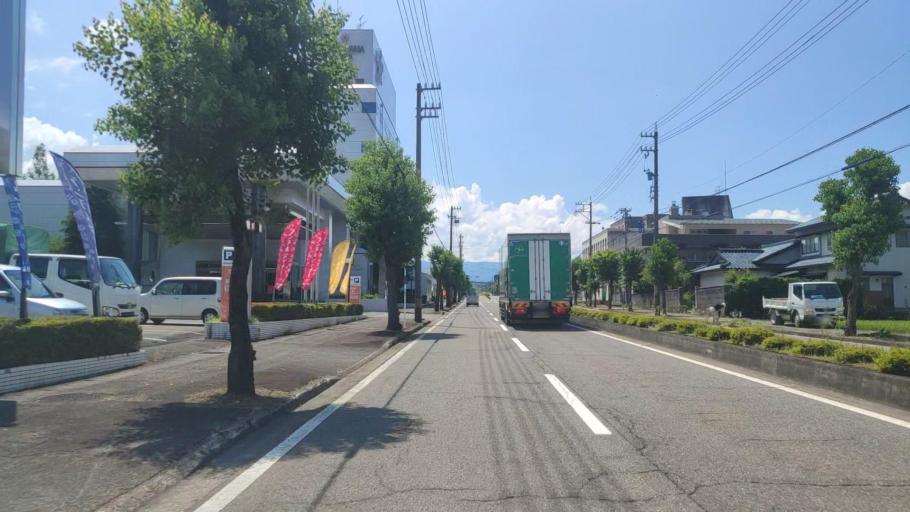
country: JP
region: Fukui
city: Katsuyama
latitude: 36.0505
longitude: 136.5143
